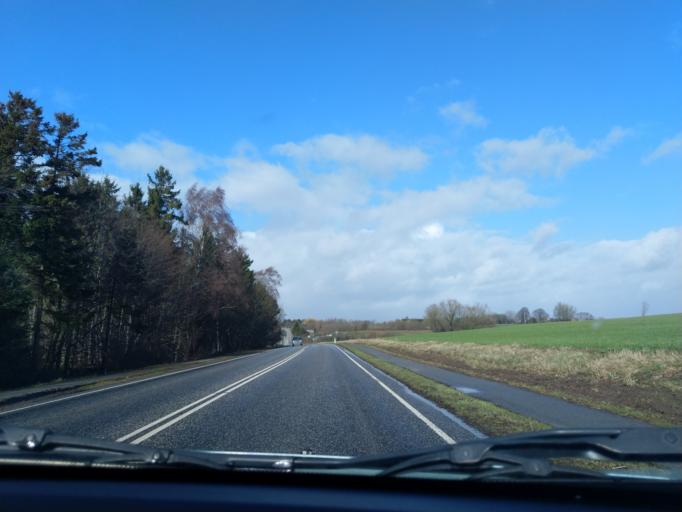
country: DK
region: Zealand
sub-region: Naestved Kommune
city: Naestved
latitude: 55.3002
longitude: 11.6918
